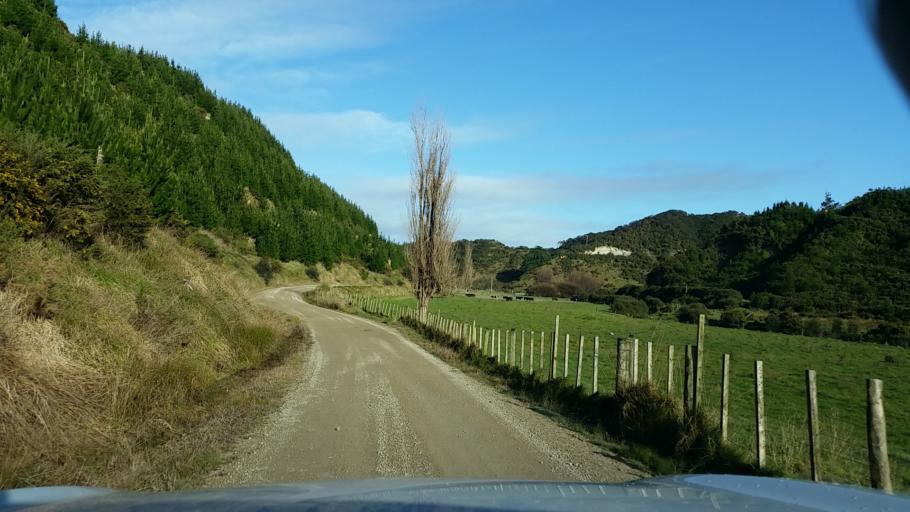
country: NZ
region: Taranaki
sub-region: South Taranaki District
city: Patea
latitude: -39.6953
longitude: 174.7446
